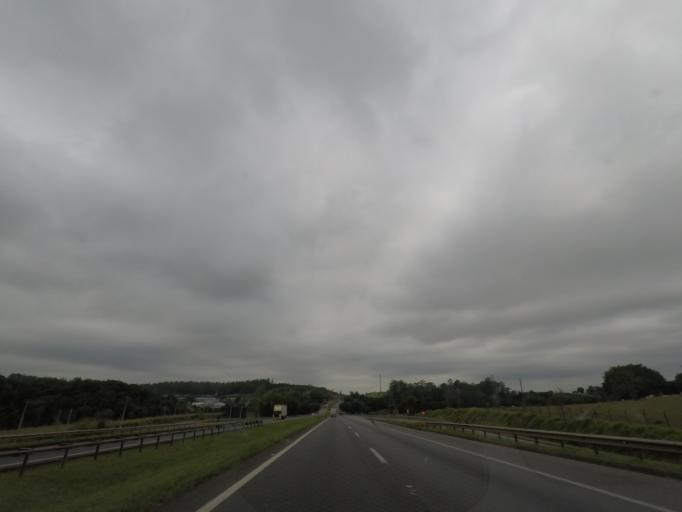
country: BR
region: Sao Paulo
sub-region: Itatiba
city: Itatiba
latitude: -22.9573
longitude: -46.8544
